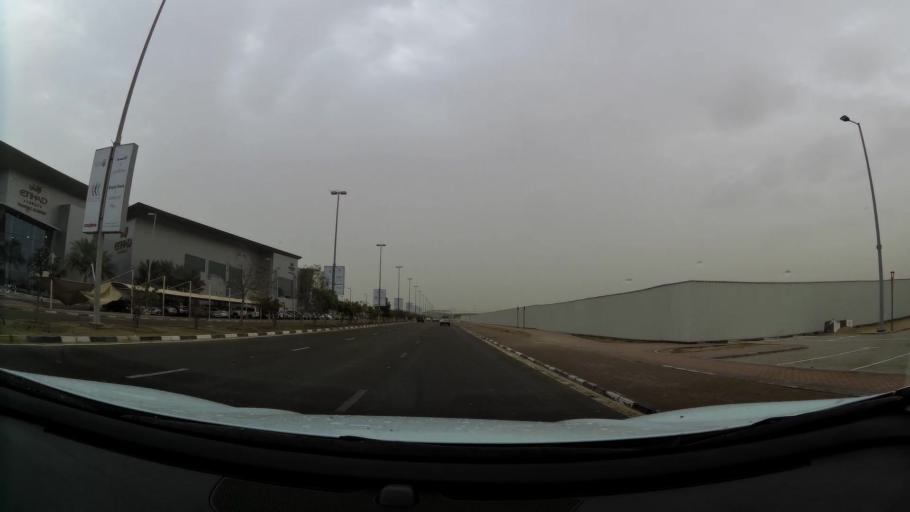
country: AE
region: Abu Dhabi
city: Abu Dhabi
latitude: 24.4446
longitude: 54.6118
